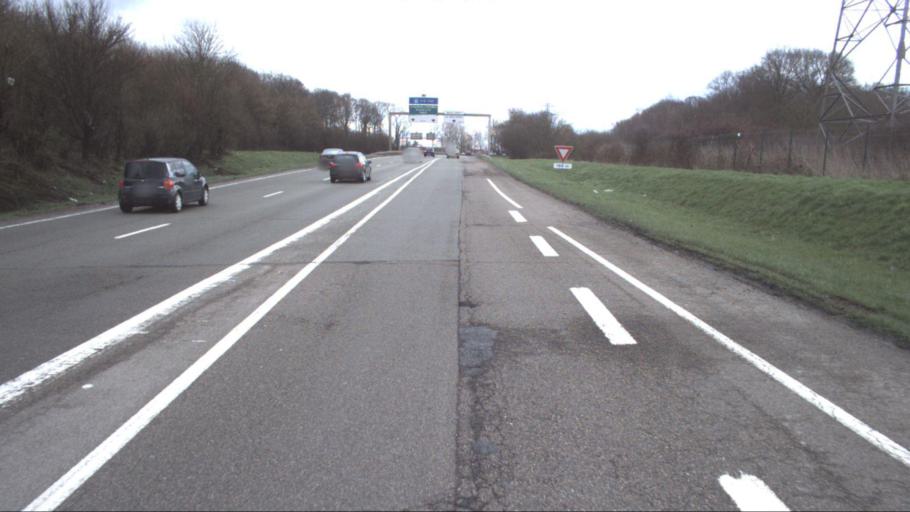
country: FR
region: Ile-de-France
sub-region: Departement des Yvelines
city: Les Clayes-sous-Bois
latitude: 48.7987
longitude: 1.9944
